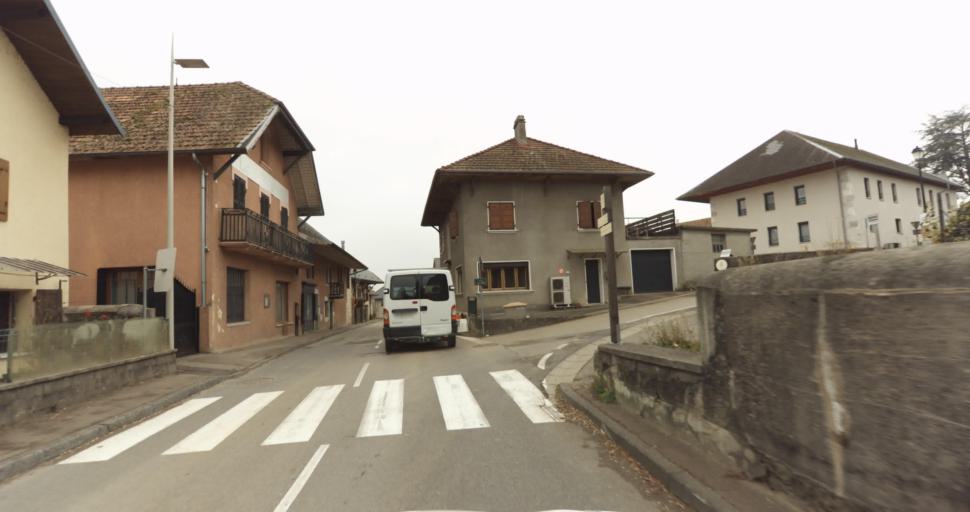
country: FR
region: Rhone-Alpes
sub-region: Departement de la Haute-Savoie
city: Alby-sur-Cheran
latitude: 45.7964
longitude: 6.0128
